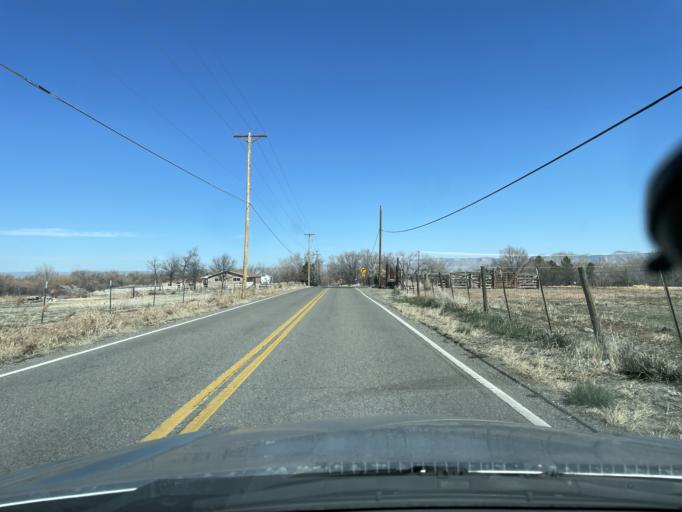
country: US
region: Colorado
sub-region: Mesa County
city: Redlands
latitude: 39.0871
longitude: -108.6688
